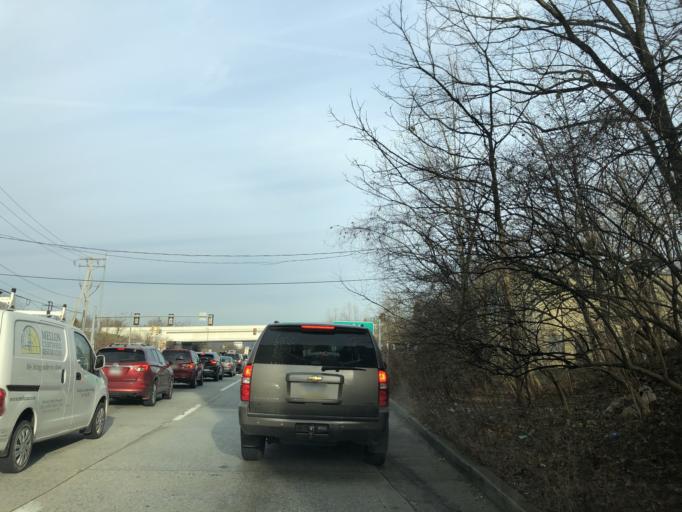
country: US
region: Pennsylvania
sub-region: Chester County
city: Exton
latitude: 40.0197
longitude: -75.6233
